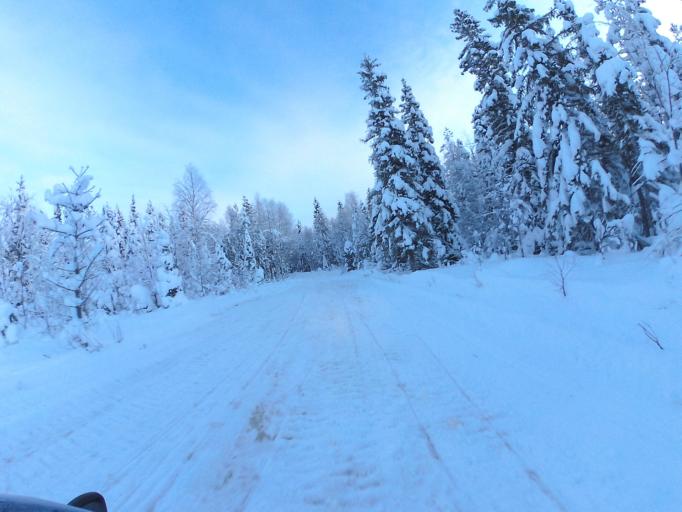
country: FI
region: Lapland
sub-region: Rovaniemi
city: Rovaniemi
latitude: 66.5186
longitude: 26.0111
